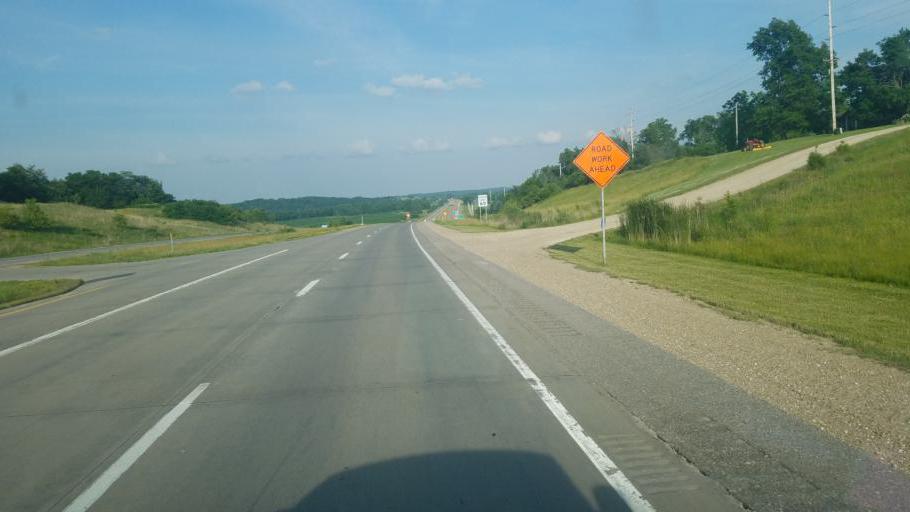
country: US
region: Iowa
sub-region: Tama County
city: Toledo
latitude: 42.0058
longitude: -92.7358
